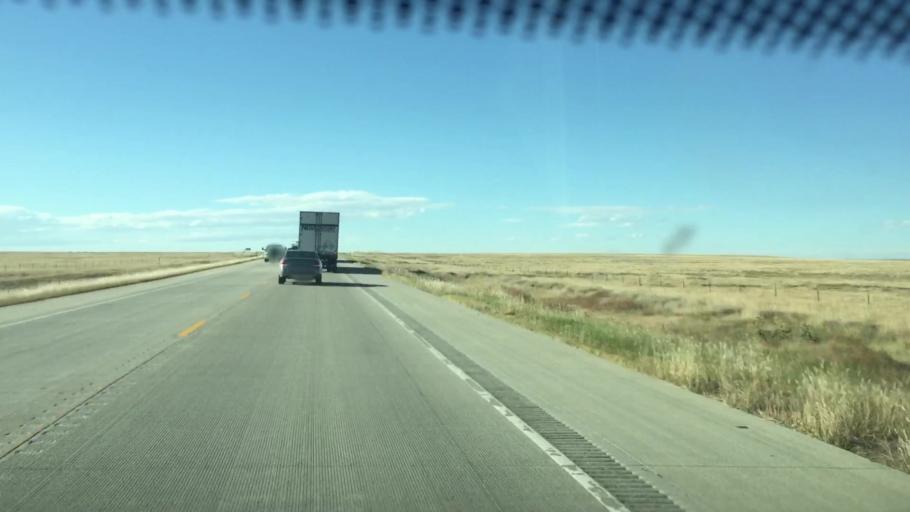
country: US
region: Colorado
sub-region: Lincoln County
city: Hugo
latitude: 38.9208
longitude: -103.1853
